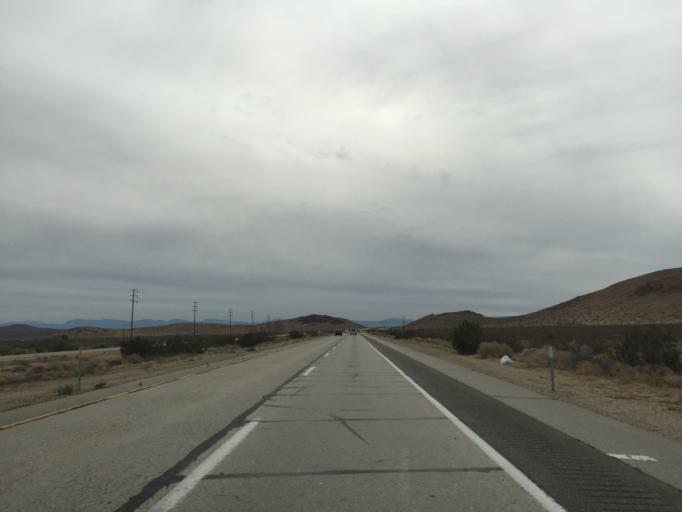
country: US
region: California
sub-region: Kern County
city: Mojave
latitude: 34.9862
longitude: -118.1594
